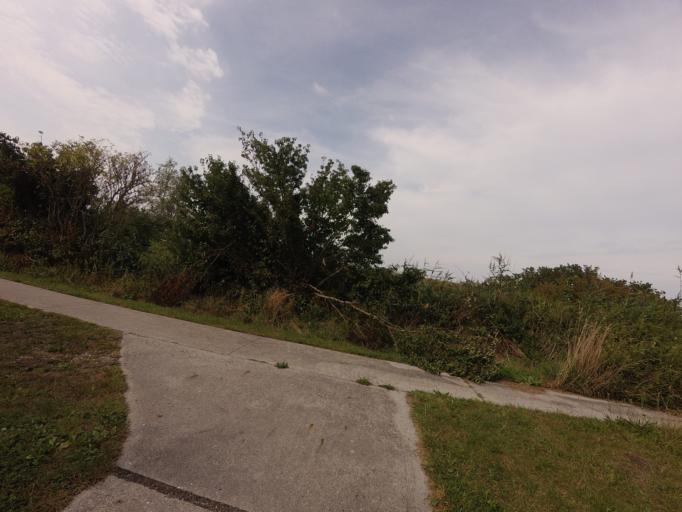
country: NL
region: Flevoland
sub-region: Gemeente Almere
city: Almere Stad
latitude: 52.4028
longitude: 5.1748
